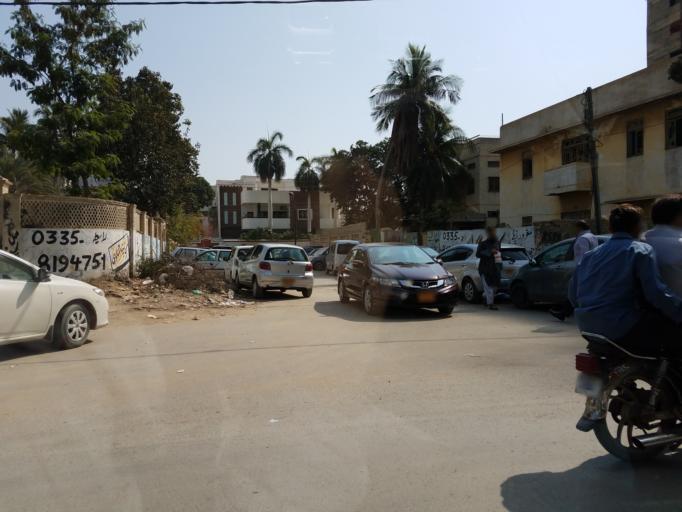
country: PK
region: Sindh
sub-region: Karachi District
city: Karachi
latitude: 24.8787
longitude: 67.0645
